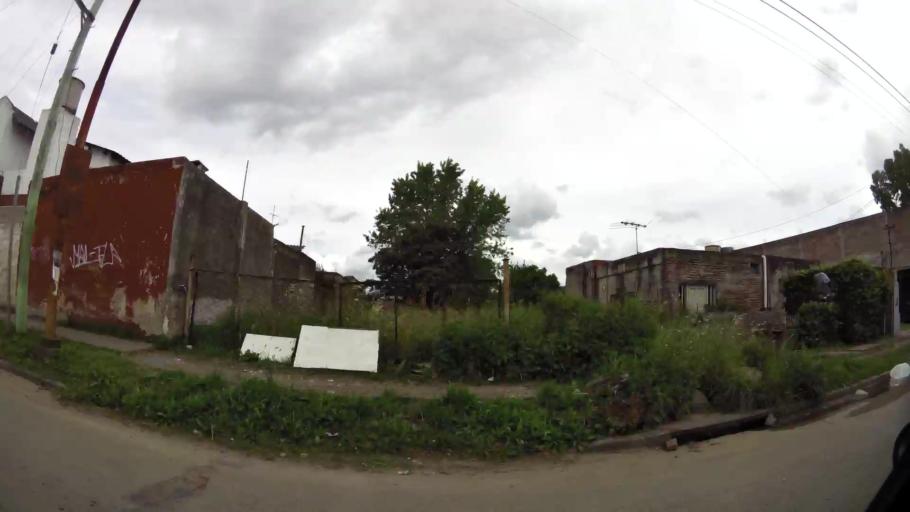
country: AR
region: Buenos Aires
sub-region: Partido de Quilmes
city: Quilmes
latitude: -34.7708
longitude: -58.2749
